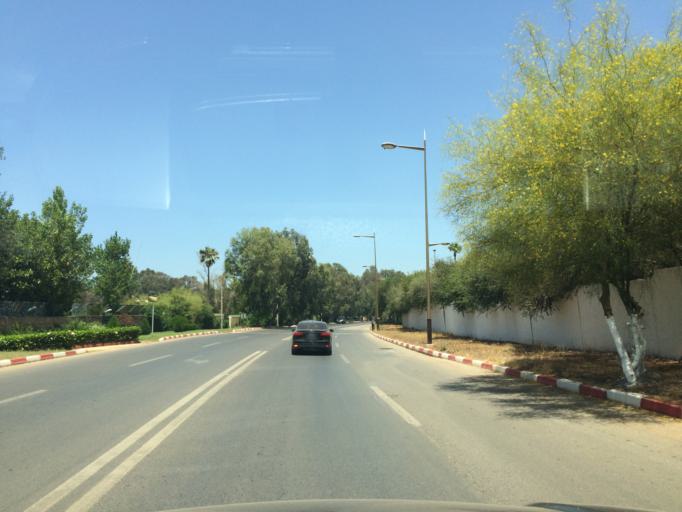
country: MA
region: Rabat-Sale-Zemmour-Zaer
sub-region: Skhirate-Temara
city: Temara
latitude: 33.9241
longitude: -6.8215
